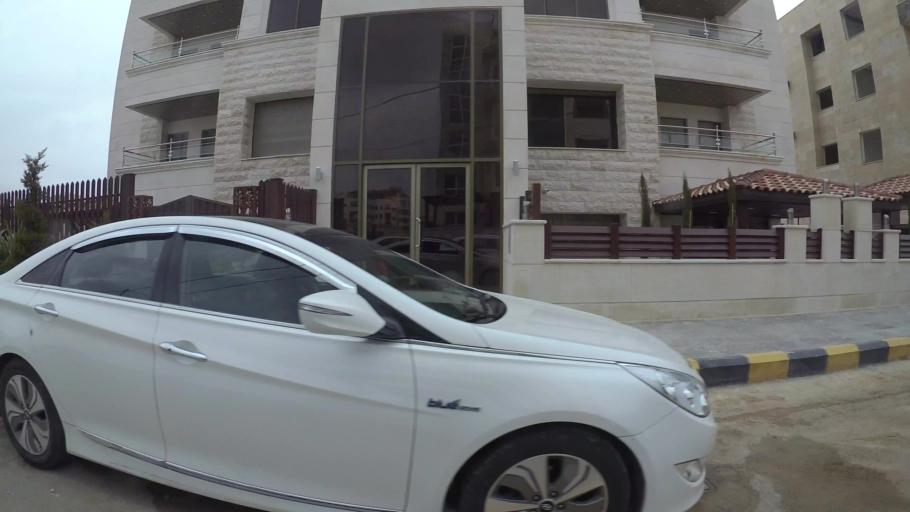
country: JO
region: Amman
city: Al Jubayhah
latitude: 31.9927
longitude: 35.8400
